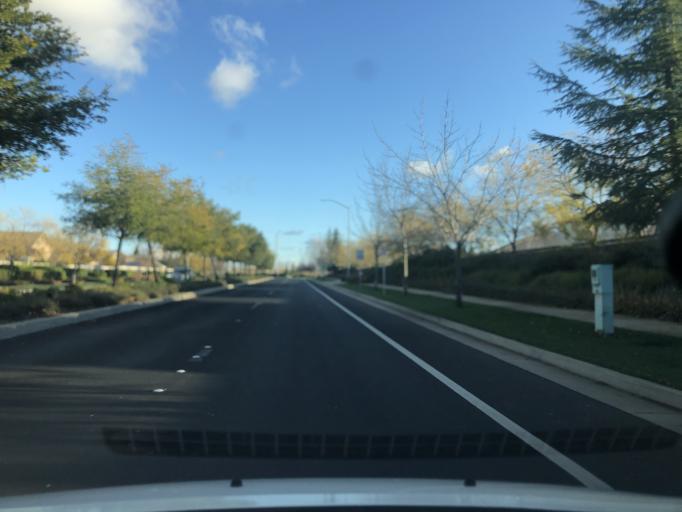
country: US
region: California
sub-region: Sacramento County
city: Antelope
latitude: 38.7682
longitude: -121.3643
